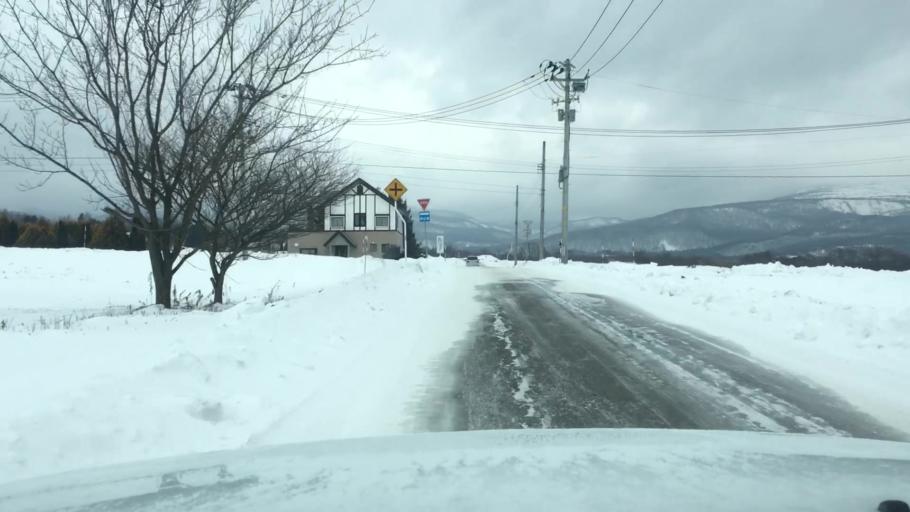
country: JP
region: Iwate
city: Shizukuishi
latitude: 39.9095
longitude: 141.0062
